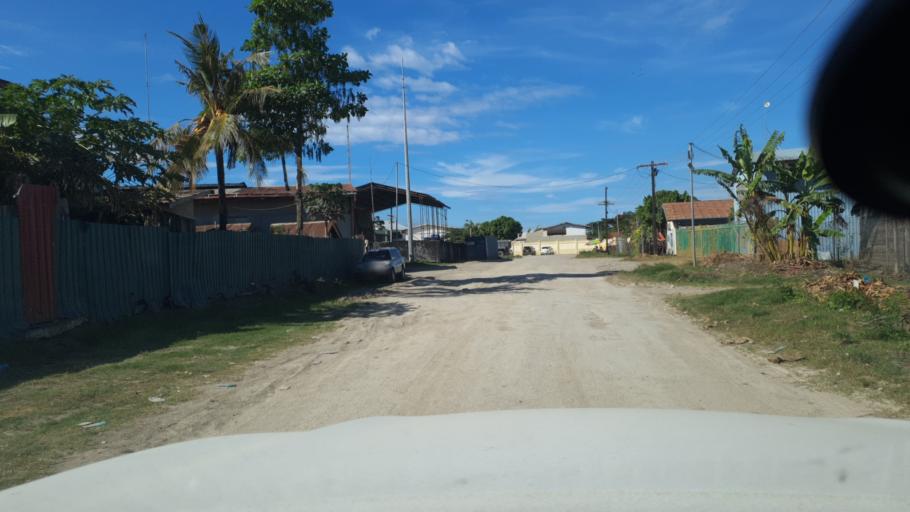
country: SB
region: Guadalcanal
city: Honiara
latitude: -9.4271
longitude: 160.0035
